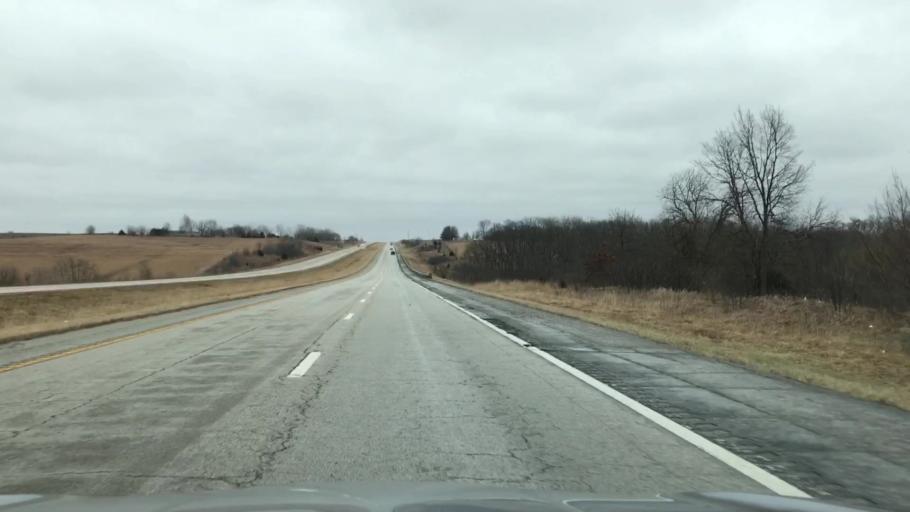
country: US
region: Missouri
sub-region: Caldwell County
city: Hamilton
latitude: 39.7499
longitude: -94.1005
